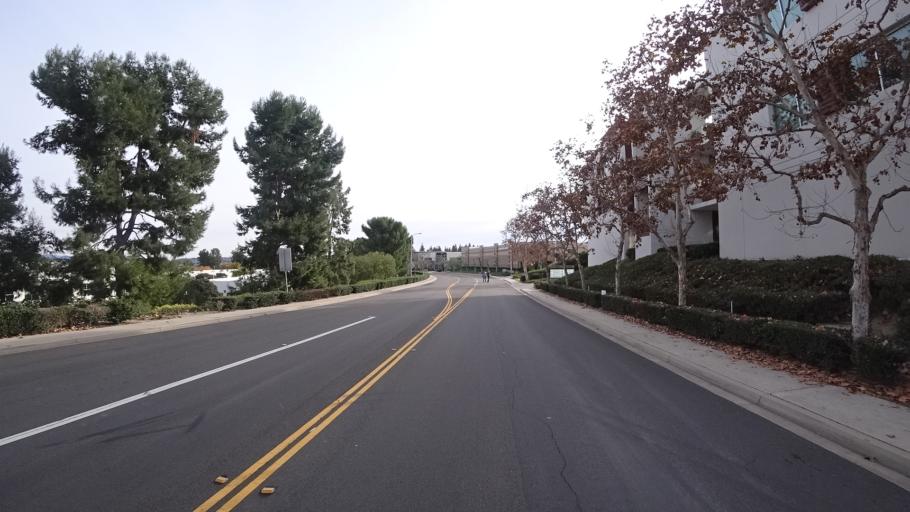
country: US
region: California
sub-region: Orange County
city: Aliso Viejo
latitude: 33.5695
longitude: -117.7264
